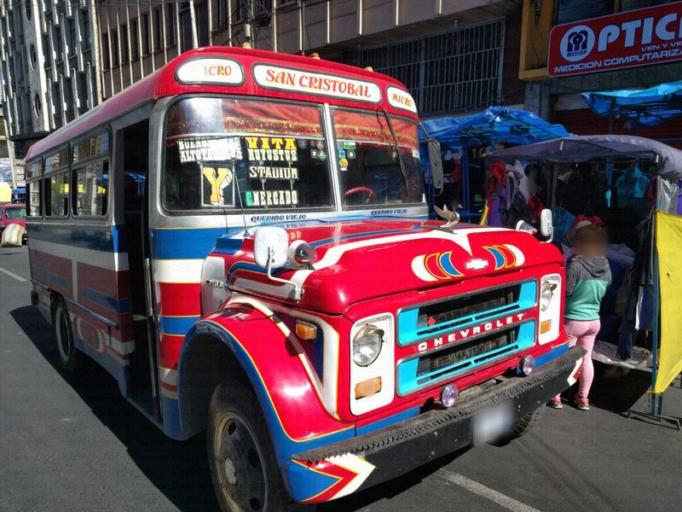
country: BO
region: La Paz
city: La Paz
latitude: -16.4950
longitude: -68.1382
